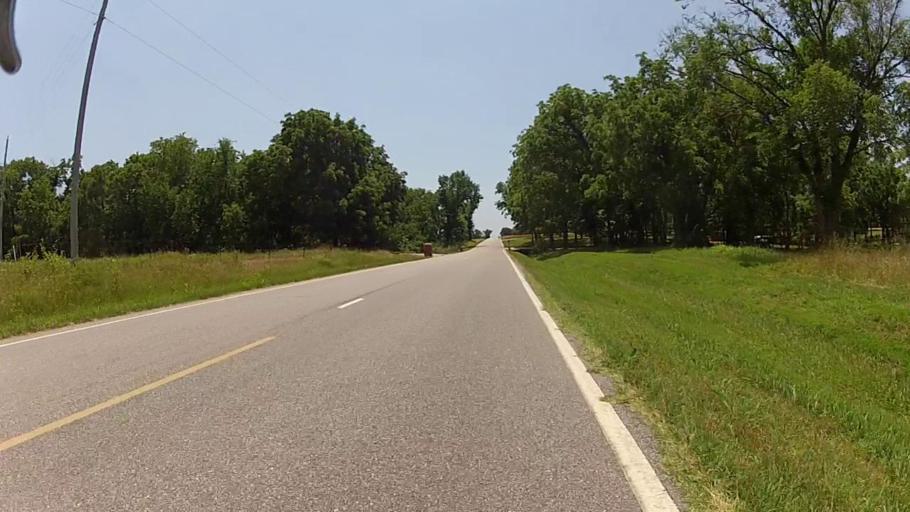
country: US
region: Kansas
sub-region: Montgomery County
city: Cherryvale
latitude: 37.2466
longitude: -95.5373
